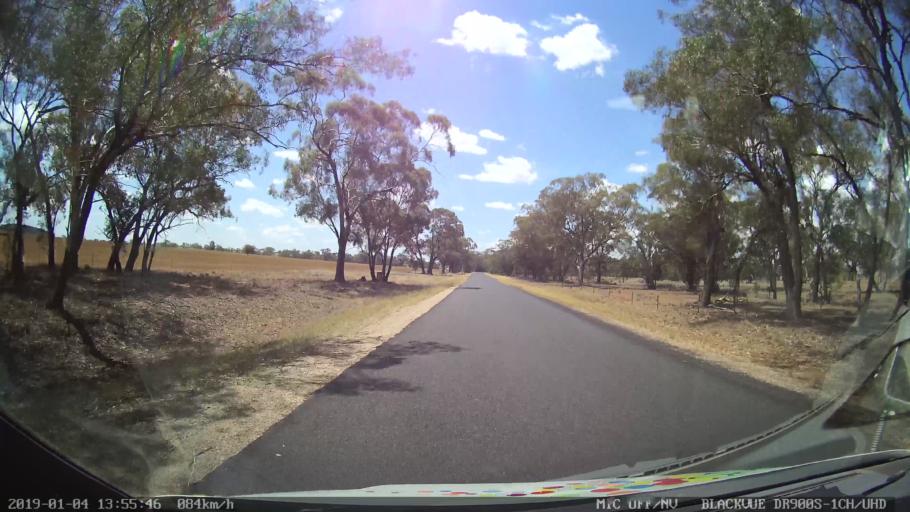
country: AU
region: New South Wales
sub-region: Dubbo Municipality
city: Dubbo
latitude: -32.3586
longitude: 148.5899
